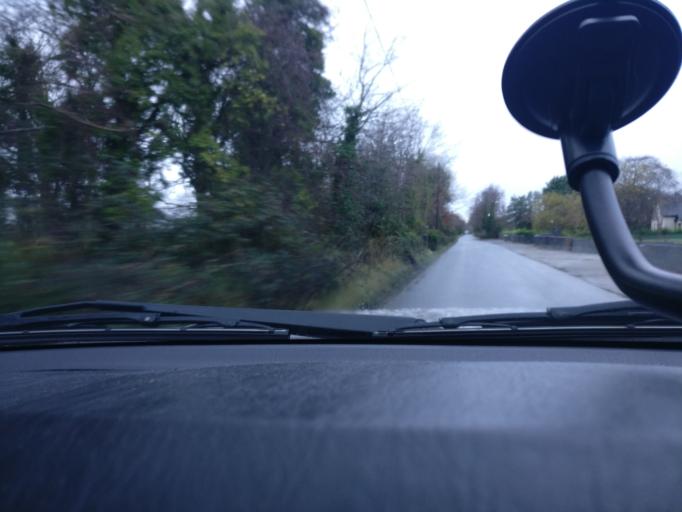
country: IE
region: Connaught
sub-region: County Galway
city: Loughrea
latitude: 53.2498
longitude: -8.5696
